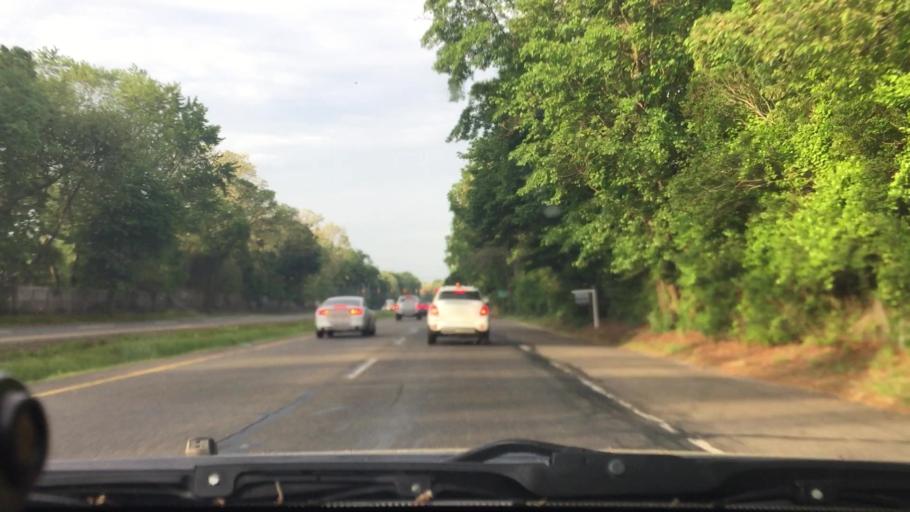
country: US
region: New York
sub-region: Suffolk County
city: Selden
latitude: 40.8773
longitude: -73.0204
